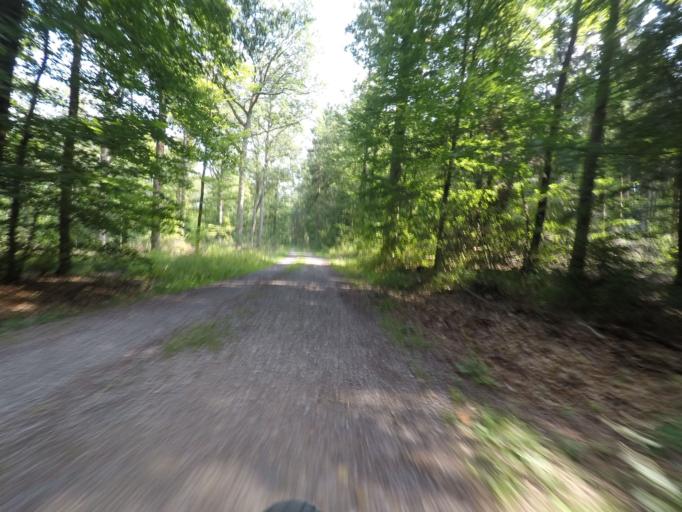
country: DE
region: Baden-Wuerttemberg
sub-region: Regierungsbezirk Stuttgart
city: Steinenbronn
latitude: 48.7020
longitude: 9.1012
